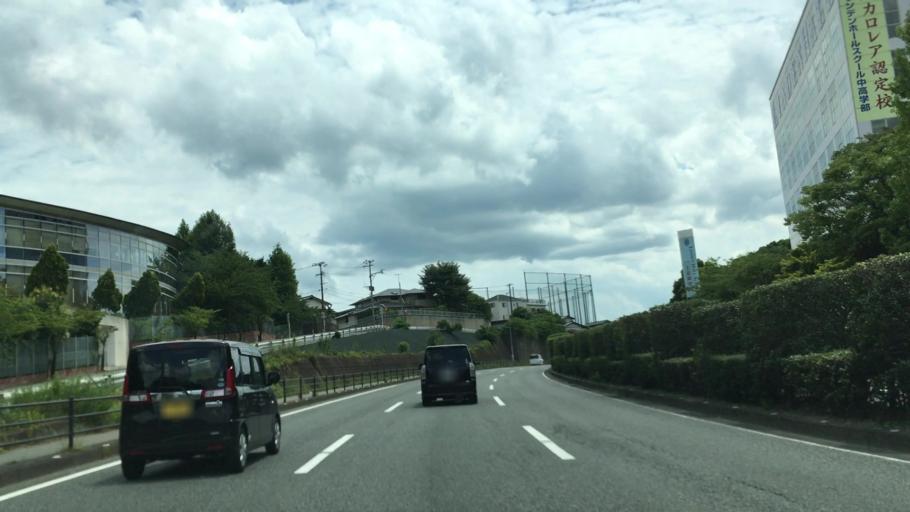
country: JP
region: Fukuoka
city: Dazaifu
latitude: 33.5063
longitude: 130.5285
